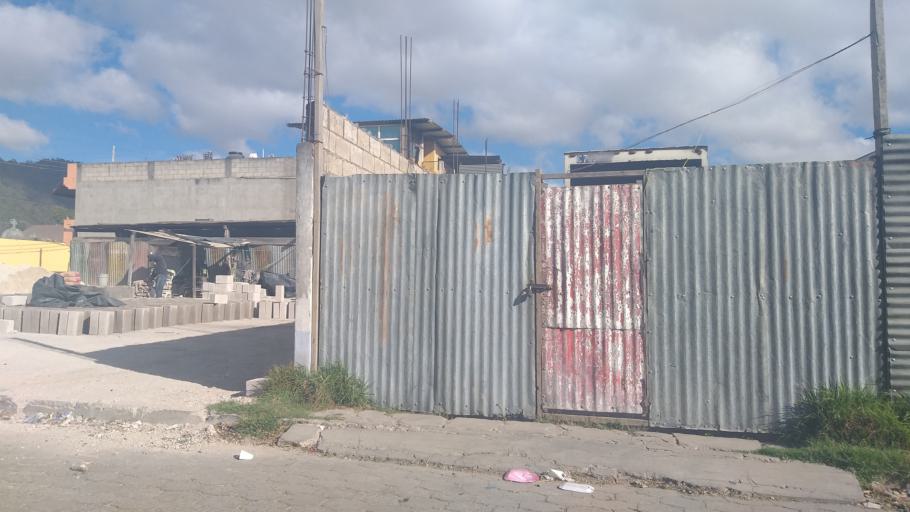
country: GT
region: Quetzaltenango
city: Ostuncalco
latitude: 14.8687
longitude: -91.6256
